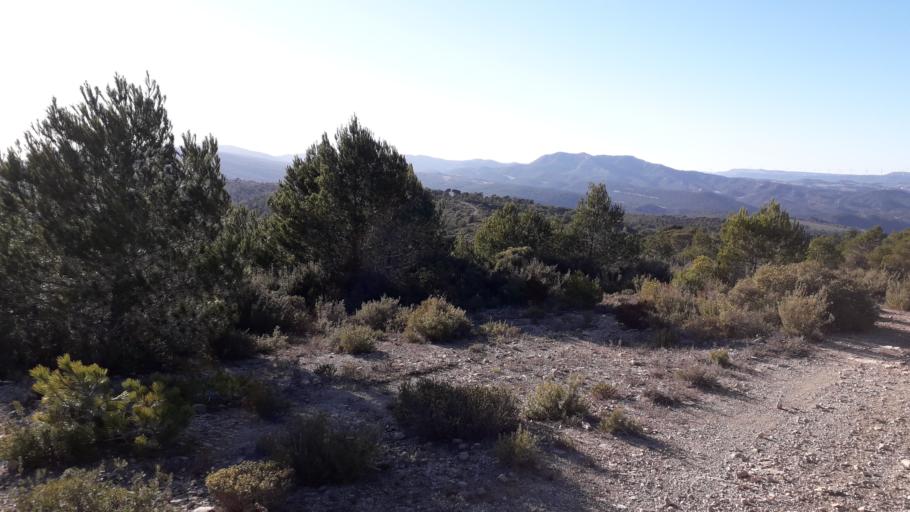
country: ES
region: Catalonia
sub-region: Provincia de Barcelona
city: Bellprat
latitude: 41.4714
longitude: 1.4262
